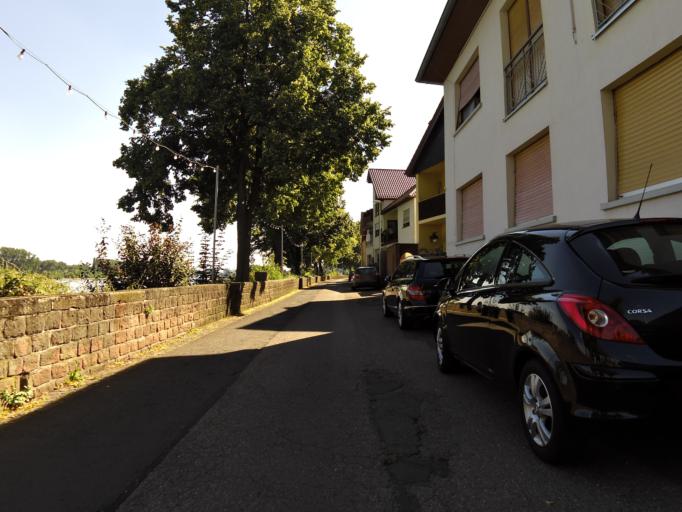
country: DE
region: Rheinland-Pfalz
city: Osthofen
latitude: 49.6970
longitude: 8.3578
